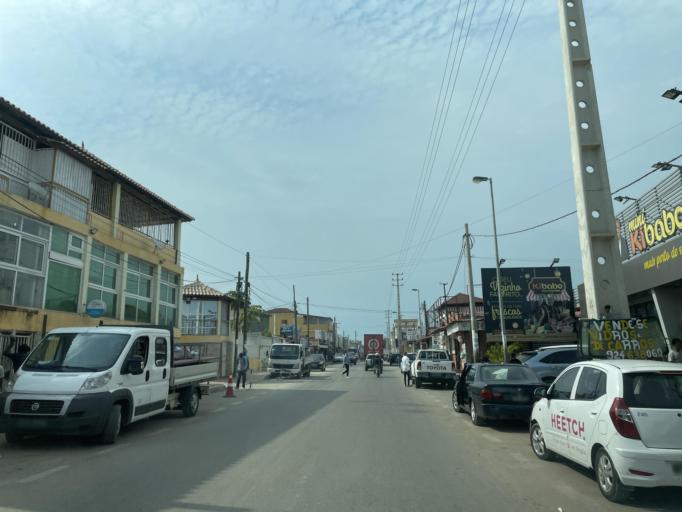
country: AO
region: Luanda
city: Luanda
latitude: -8.9004
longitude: 13.1871
